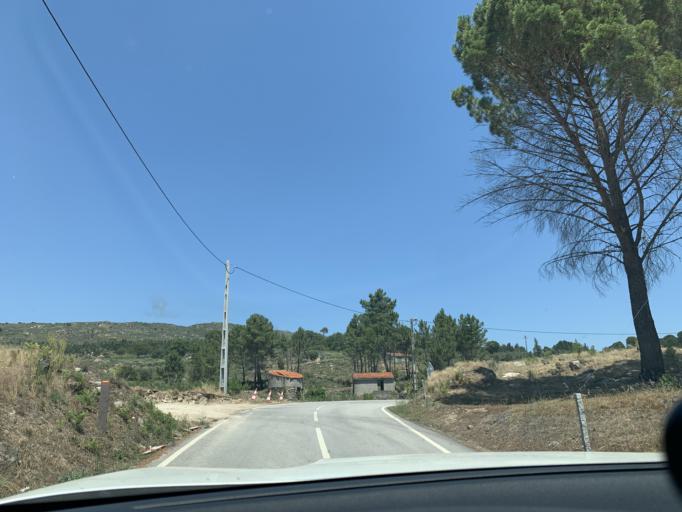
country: PT
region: Viseu
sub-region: Mangualde
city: Mangualde
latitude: 40.5730
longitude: -7.6474
